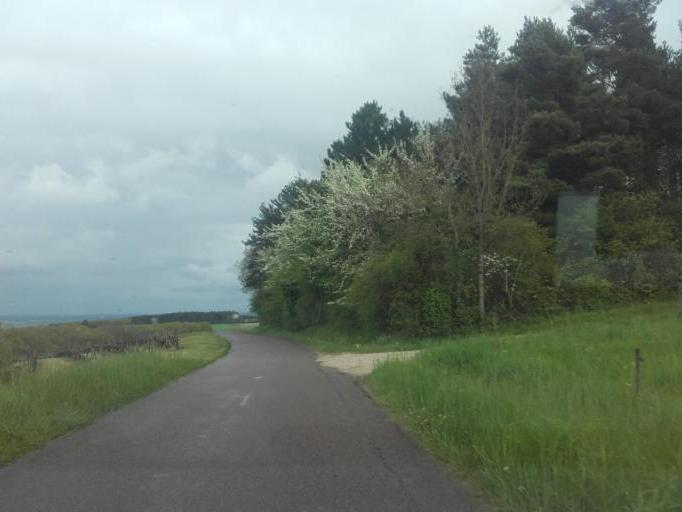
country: FR
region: Bourgogne
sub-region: Departement de la Cote-d'Or
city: Nuits-Saint-Georges
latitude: 47.1046
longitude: 4.8835
